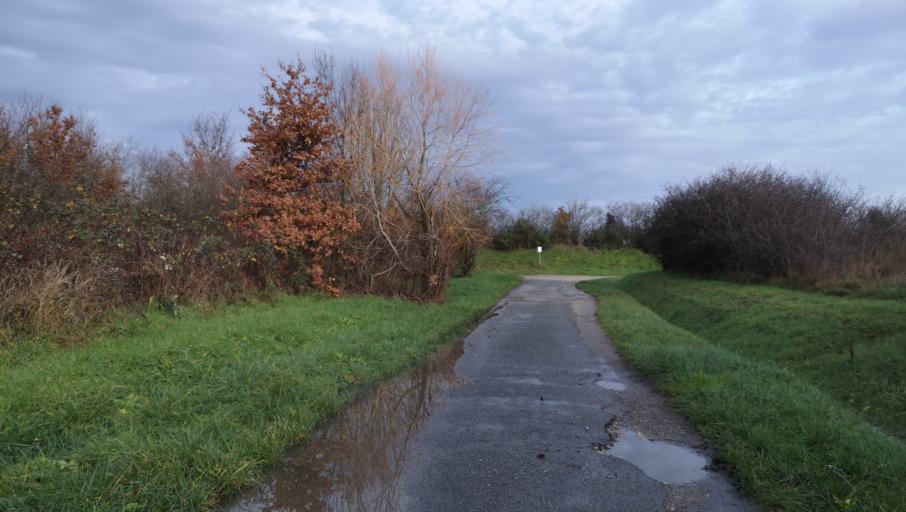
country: FR
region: Centre
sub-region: Departement du Loiret
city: Saint-Jean-de-Braye
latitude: 47.9241
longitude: 1.9675
